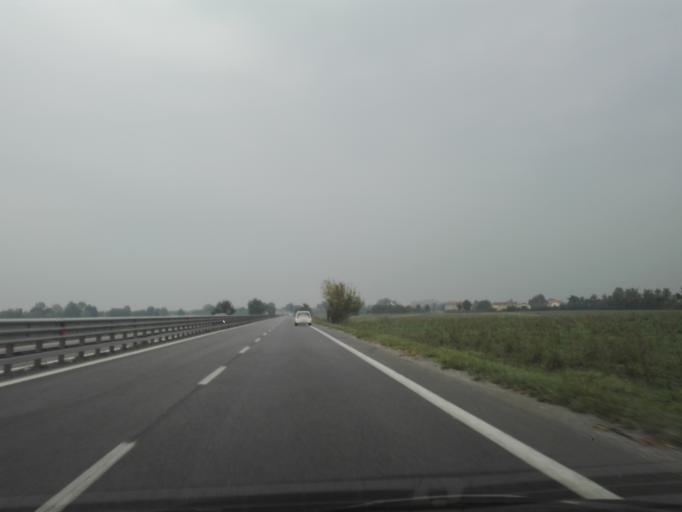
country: IT
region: Veneto
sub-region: Provincia di Verona
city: Legnago
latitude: 45.1700
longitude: 11.2944
